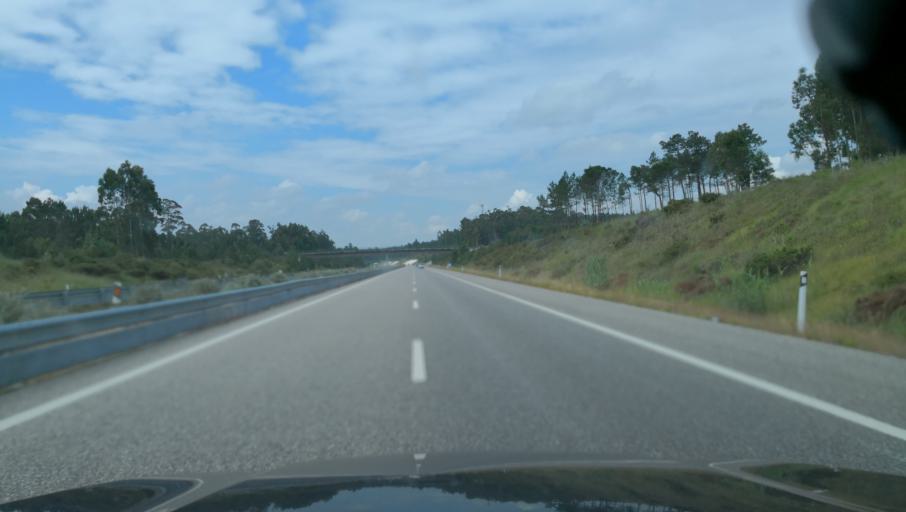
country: PT
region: Leiria
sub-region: Leiria
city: Amor
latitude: 39.7916
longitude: -8.8606
